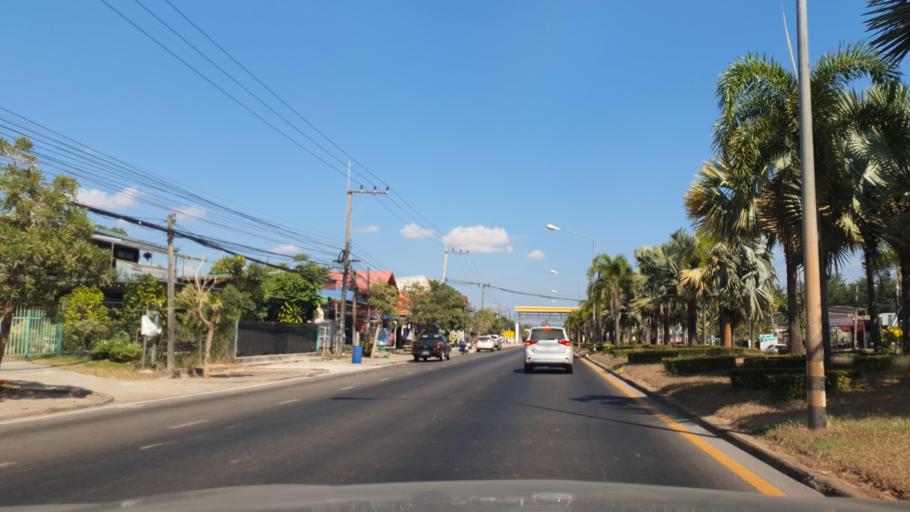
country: TH
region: Kalasin
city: Somdet
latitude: 16.7052
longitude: 103.7489
